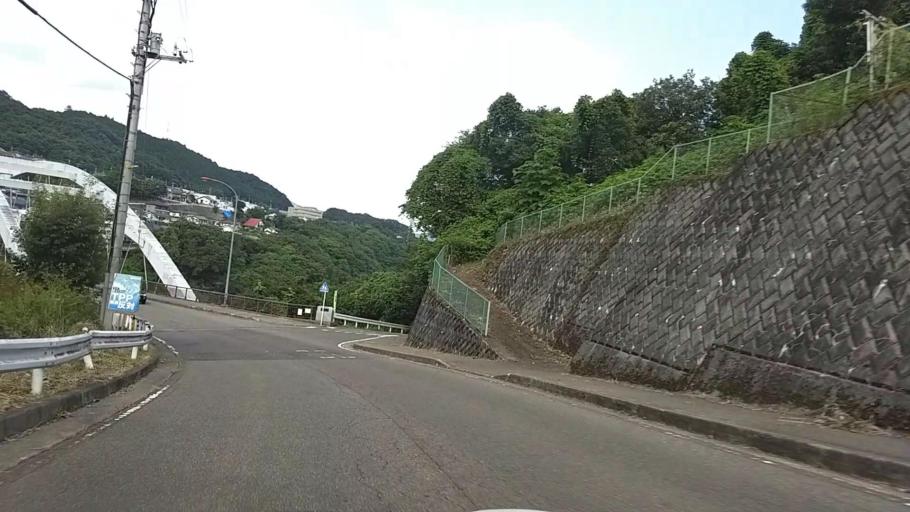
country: JP
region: Yamanashi
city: Uenohara
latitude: 35.6137
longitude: 139.1470
